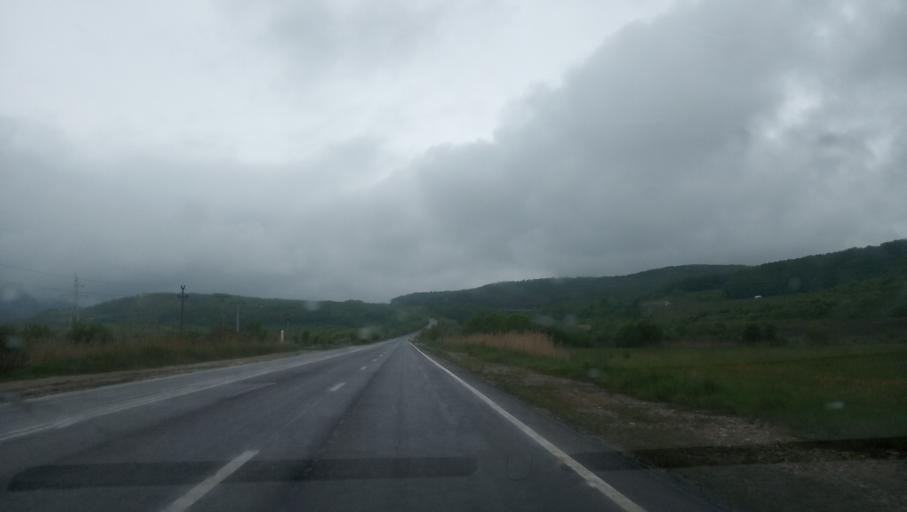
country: RO
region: Sibiu
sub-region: Comuna Orlat
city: Orlat
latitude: 45.7829
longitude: 23.9864
